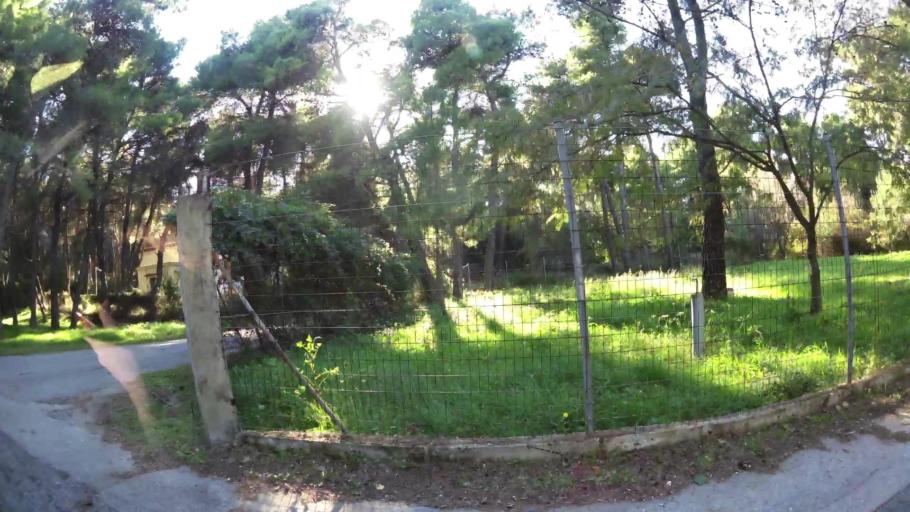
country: GR
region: Attica
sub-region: Nomarchia Anatolikis Attikis
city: Anoixi
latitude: 38.1263
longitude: 23.8490
